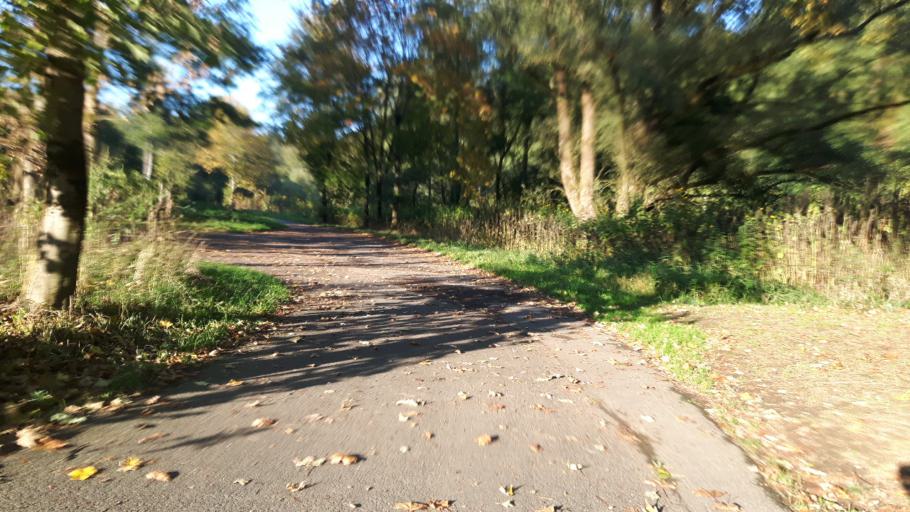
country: DE
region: Rheinland-Pfalz
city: Werkhausen
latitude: 50.7956
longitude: 7.5387
